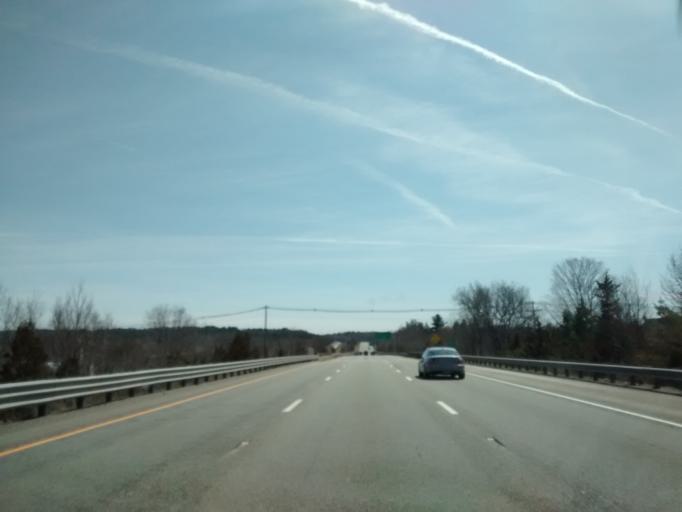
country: US
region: Massachusetts
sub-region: Worcester County
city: Cordaville
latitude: 42.2772
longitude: -71.5664
